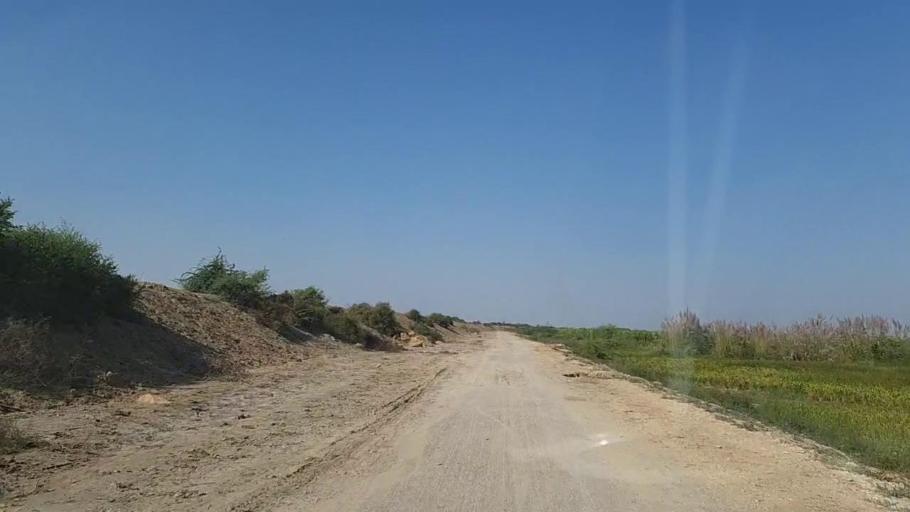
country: PK
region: Sindh
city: Chuhar Jamali
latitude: 24.5723
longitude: 68.0302
